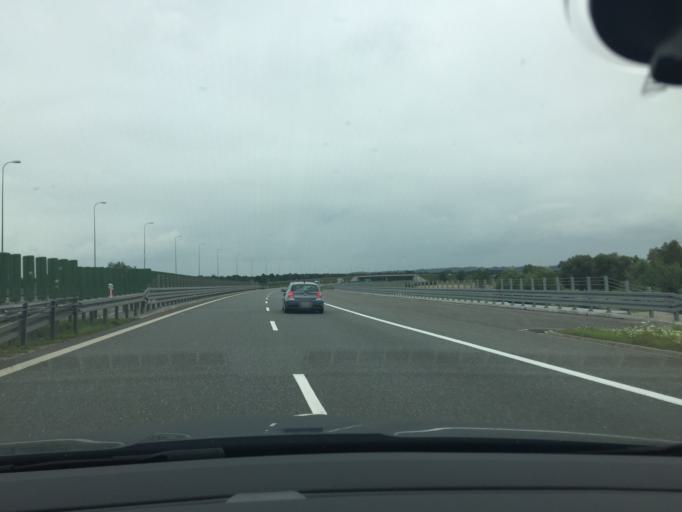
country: PL
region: Kujawsko-Pomorskie
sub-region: Grudziadz
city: Grudziadz
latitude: 53.4338
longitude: 18.6912
